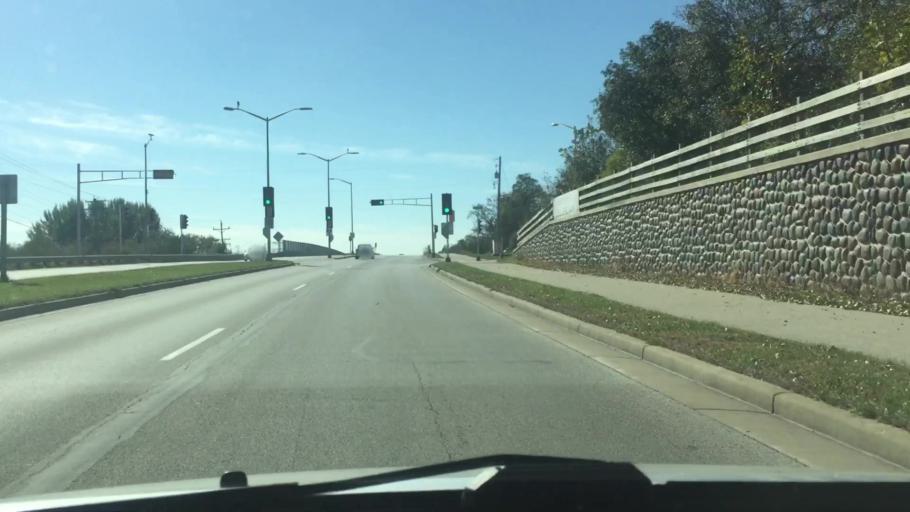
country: US
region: Wisconsin
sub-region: Waukesha County
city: Waukesha
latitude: 43.0007
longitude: -88.2555
